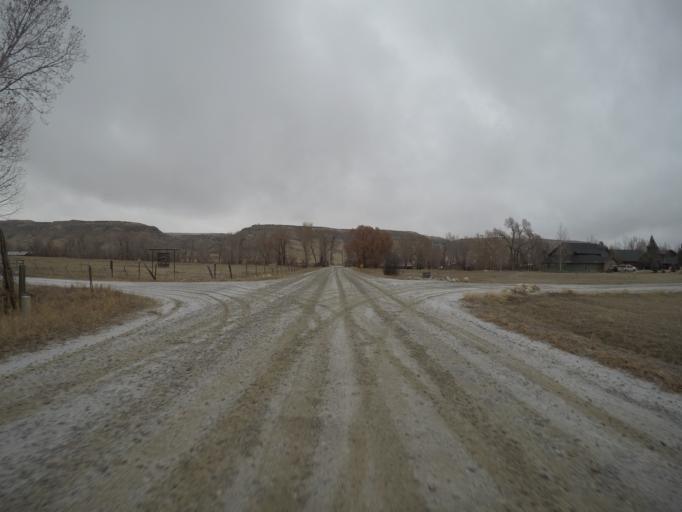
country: US
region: Montana
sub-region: Stillwater County
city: Absarokee
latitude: 45.5270
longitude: -109.4694
